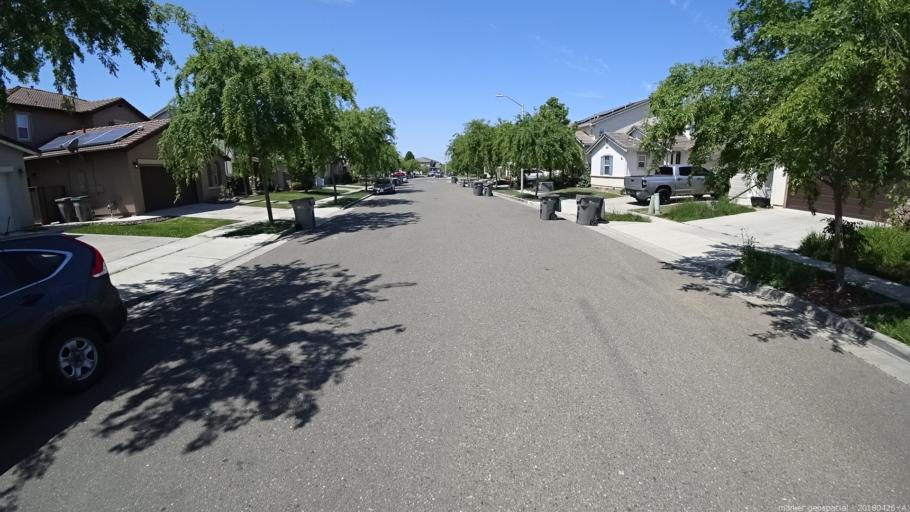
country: US
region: California
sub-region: Yolo County
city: West Sacramento
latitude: 38.5247
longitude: -121.5787
